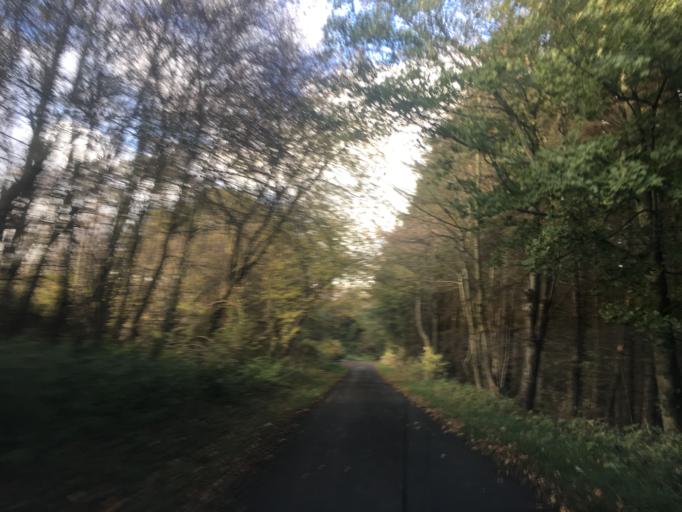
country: GB
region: Scotland
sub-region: East Lothian
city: Pencaitland
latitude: 55.8616
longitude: -2.8641
